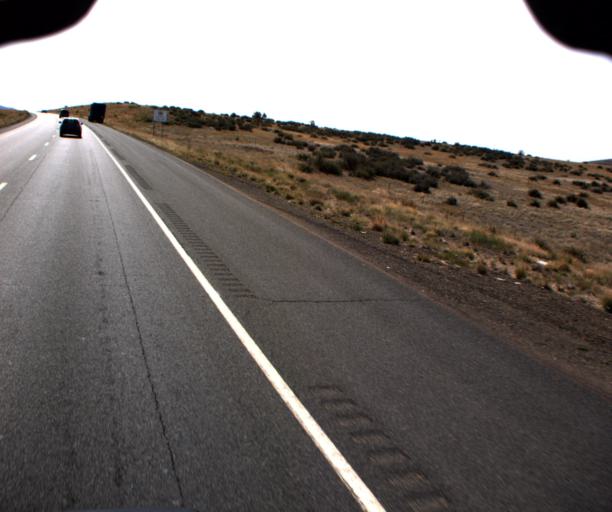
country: US
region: Arizona
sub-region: Yavapai County
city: Prescott Valley
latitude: 34.6317
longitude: -112.3889
